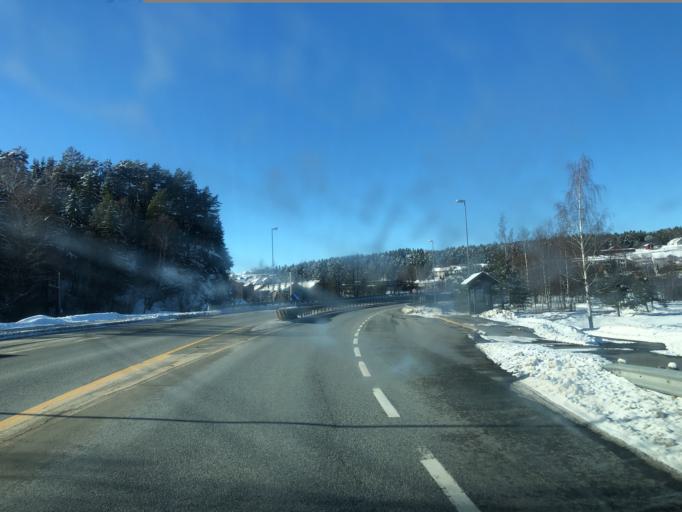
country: NO
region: Buskerud
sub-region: Hole
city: Vik
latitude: 60.0778
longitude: 10.2883
